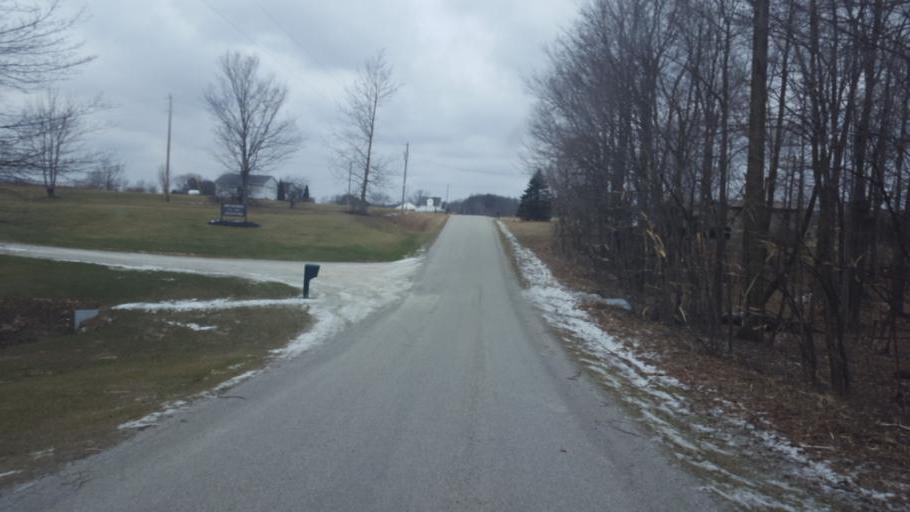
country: US
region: Ohio
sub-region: Crawford County
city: Galion
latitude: 40.6619
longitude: -82.7088
